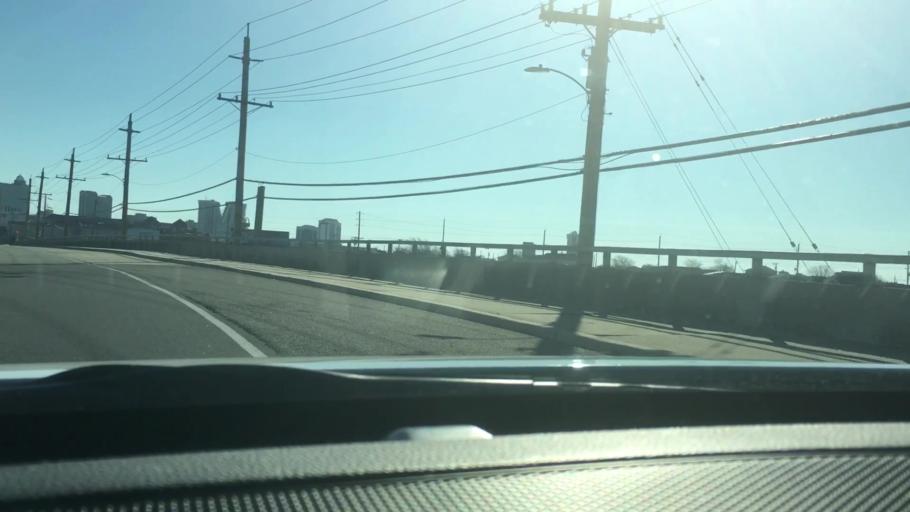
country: US
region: New Jersey
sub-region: Atlantic County
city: Ventnor City
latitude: 39.3616
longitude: -74.4652
